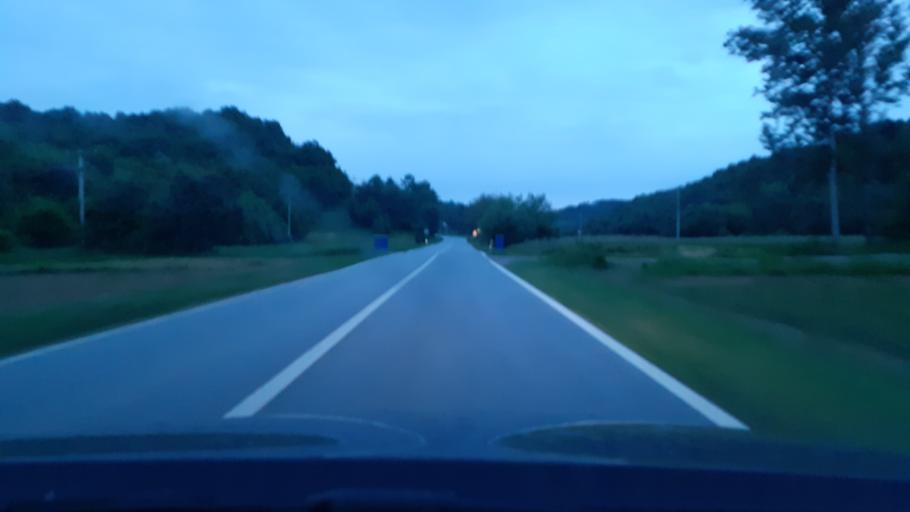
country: HR
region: Pozesko-Slavonska
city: Bilice
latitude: 45.2124
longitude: 17.8503
